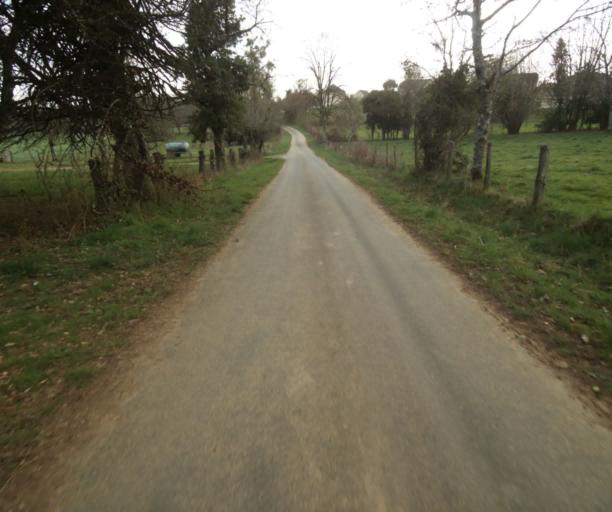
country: FR
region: Limousin
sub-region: Departement de la Correze
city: Saint-Clement
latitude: 45.3563
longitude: 1.6431
